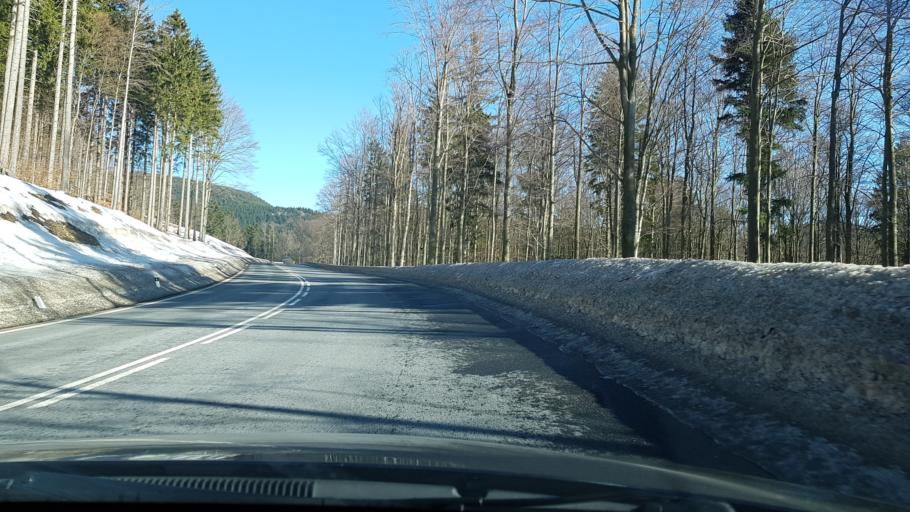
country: CZ
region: Olomoucky
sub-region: Okres Sumperk
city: Loucna nad Desnou
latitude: 50.1125
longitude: 17.1482
